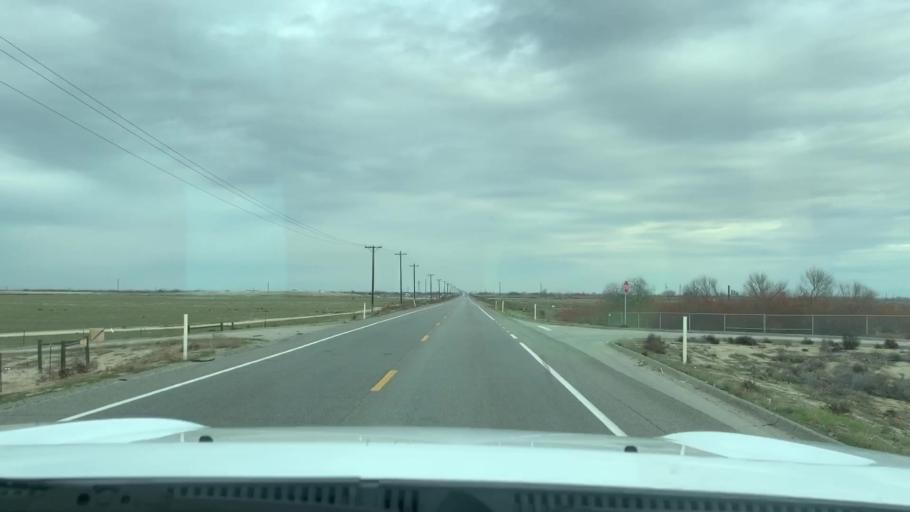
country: US
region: California
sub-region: Kern County
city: Rosedale
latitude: 35.3059
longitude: -119.2524
